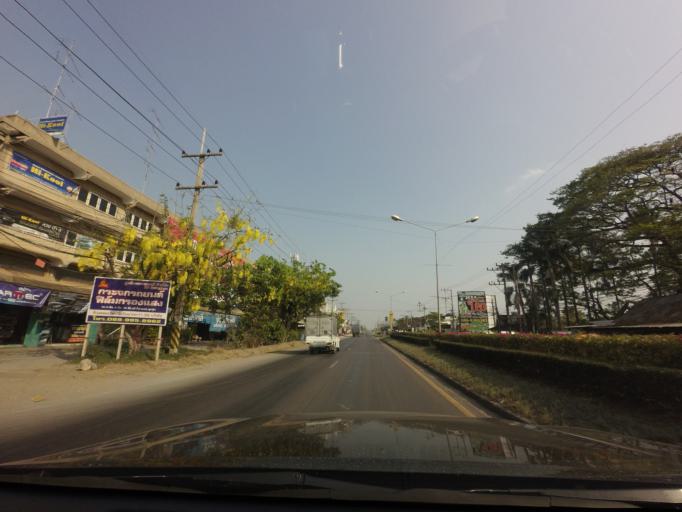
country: TH
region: Kanchanaburi
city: Tha Maka
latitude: 13.8657
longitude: 99.8255
